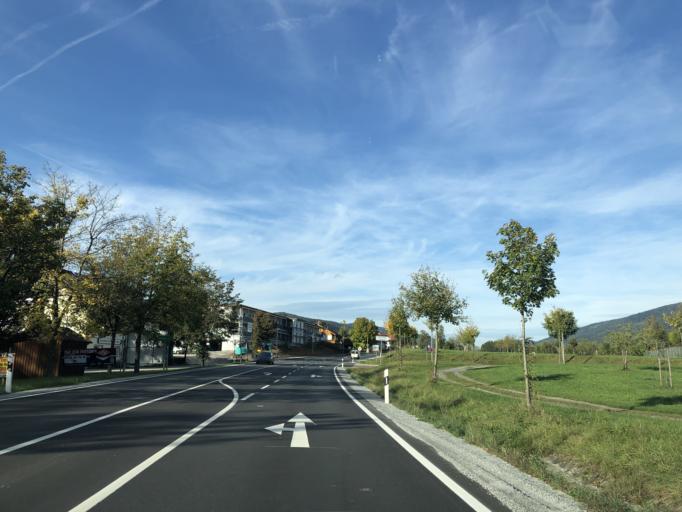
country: DE
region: Bavaria
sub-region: Lower Bavaria
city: Deggendorf
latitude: 48.8619
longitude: 12.9585
